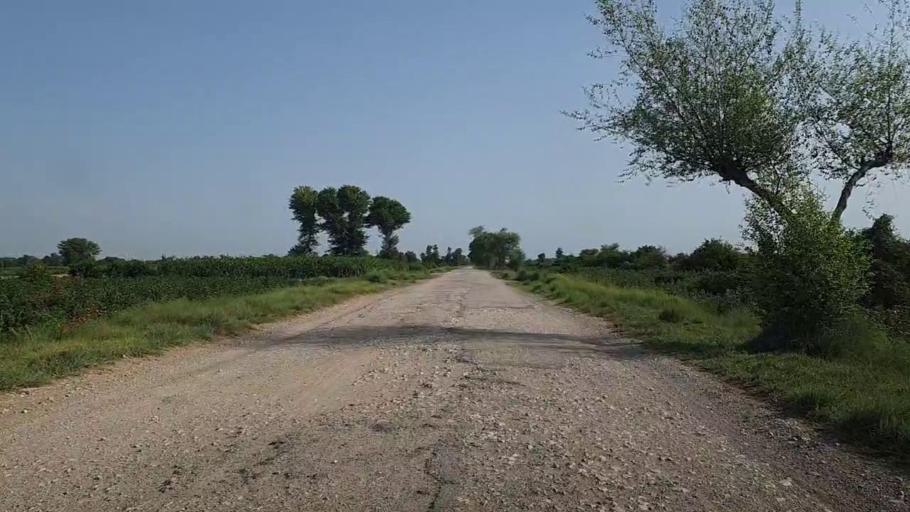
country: PK
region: Sindh
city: Karaundi
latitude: 26.8653
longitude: 68.3308
